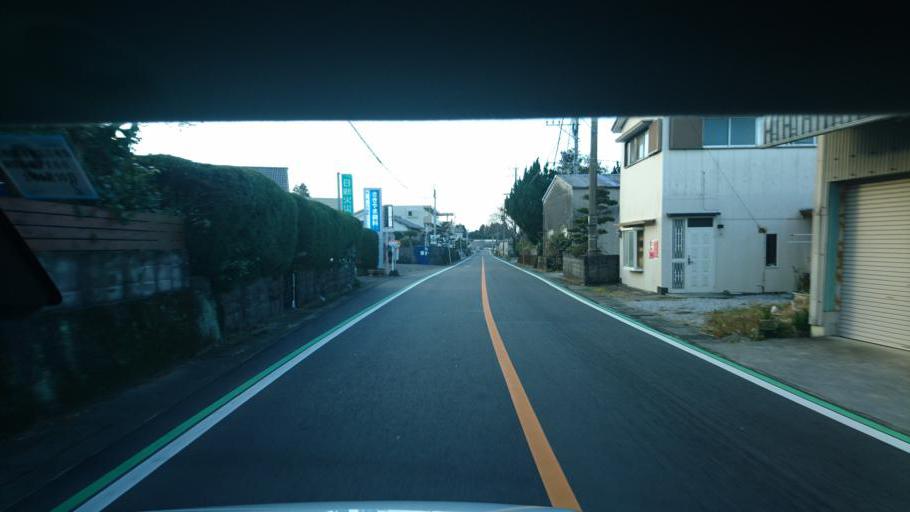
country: JP
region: Miyazaki
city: Miyazaki-shi
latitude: 31.8343
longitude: 131.4327
